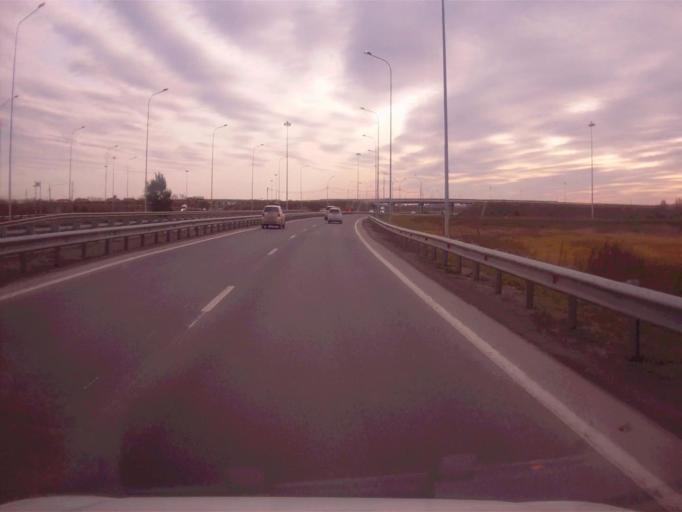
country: RU
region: Chelyabinsk
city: Novosineglazovskiy
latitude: 55.0051
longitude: 61.4538
